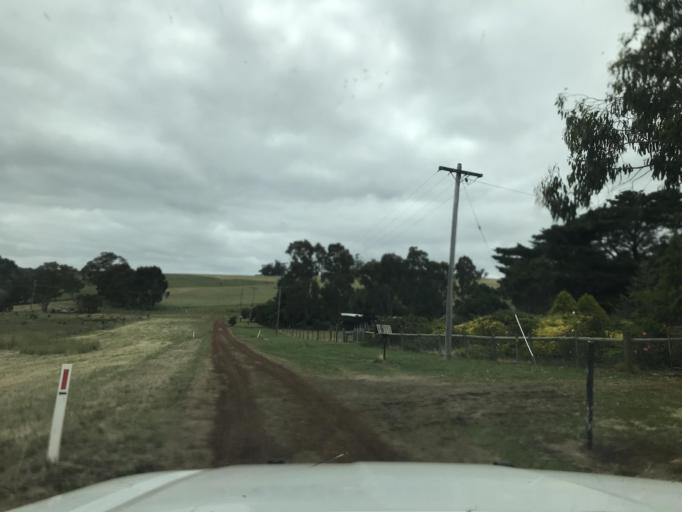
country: AU
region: South Australia
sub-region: Wattle Range
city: Penola
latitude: -37.2795
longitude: 141.4188
